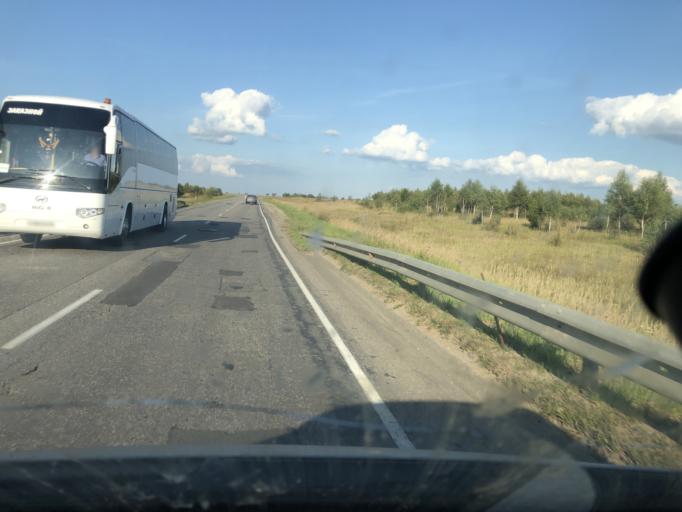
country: RU
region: Kaluga
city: Kozel'sk
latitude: 54.0671
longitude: 35.7971
